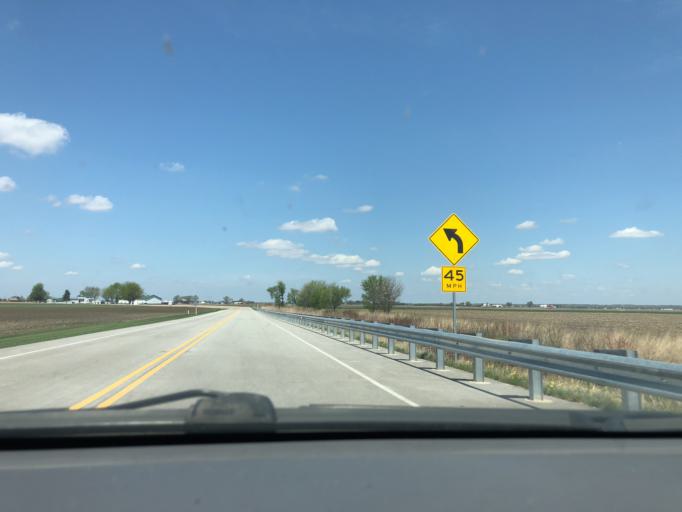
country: US
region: Illinois
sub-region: Kane County
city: Hampshire
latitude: 42.1074
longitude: -88.5561
